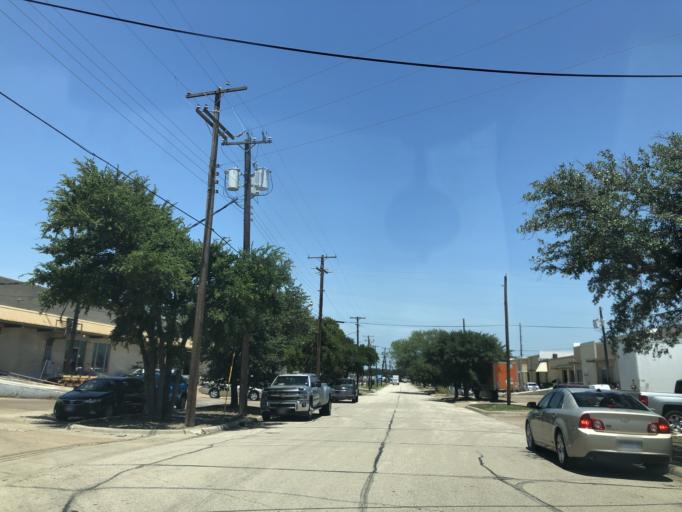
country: US
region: Texas
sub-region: Dallas County
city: Irving
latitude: 32.8042
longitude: -96.8839
